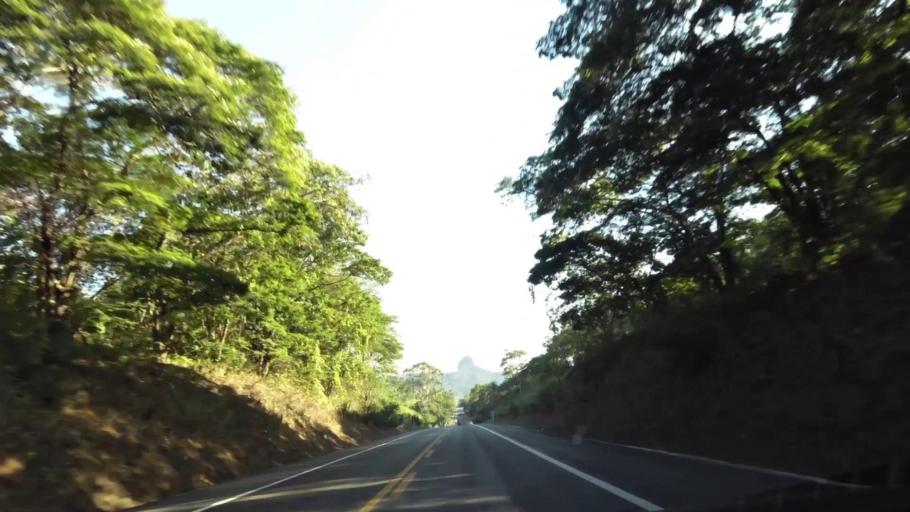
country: BR
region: Espirito Santo
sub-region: Guarapari
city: Guarapari
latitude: -20.5470
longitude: -40.4814
